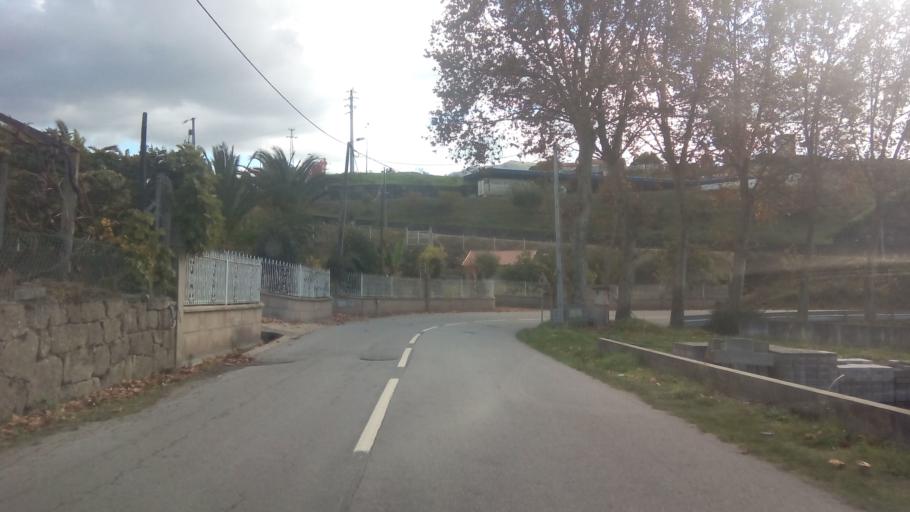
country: PT
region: Porto
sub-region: Amarante
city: Amarante
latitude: 41.2563
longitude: -8.0285
